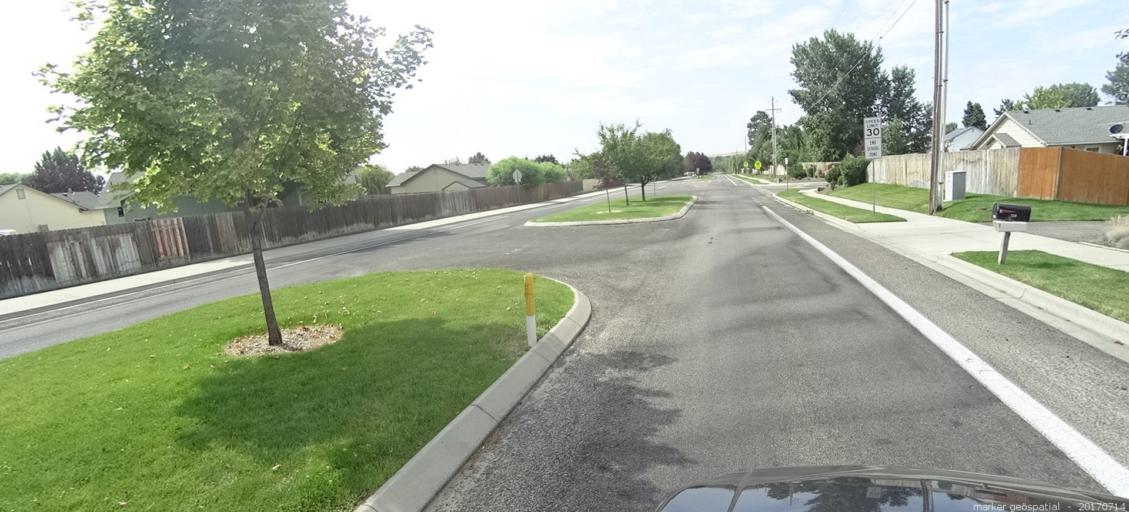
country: US
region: Idaho
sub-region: Ada County
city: Kuna
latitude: 43.4950
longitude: -116.4337
